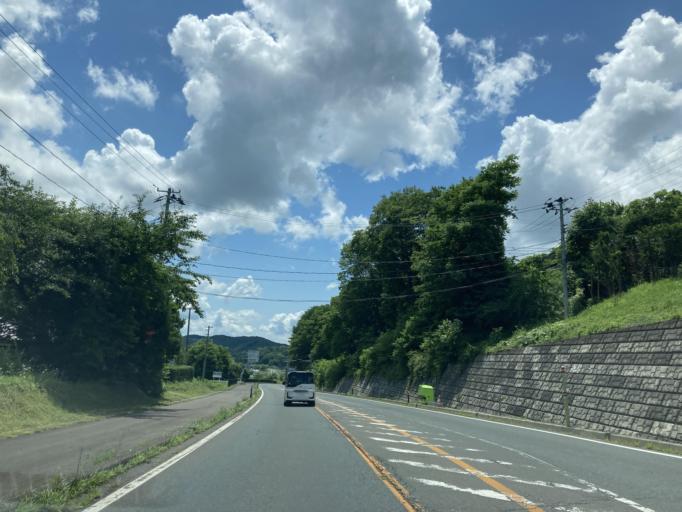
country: JP
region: Iwate
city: Ichinohe
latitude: 39.9723
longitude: 141.2145
